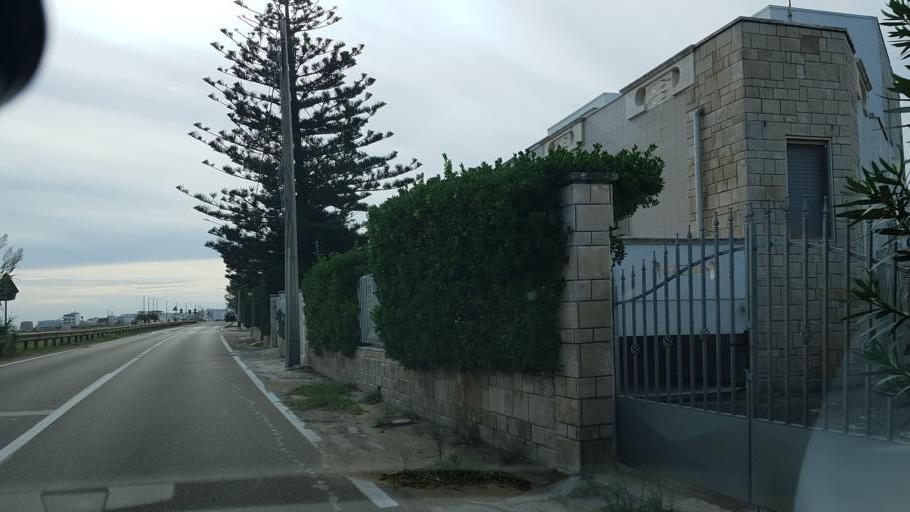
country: IT
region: Apulia
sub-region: Provincia di Lecce
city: Melendugno
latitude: 40.3072
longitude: 18.3967
